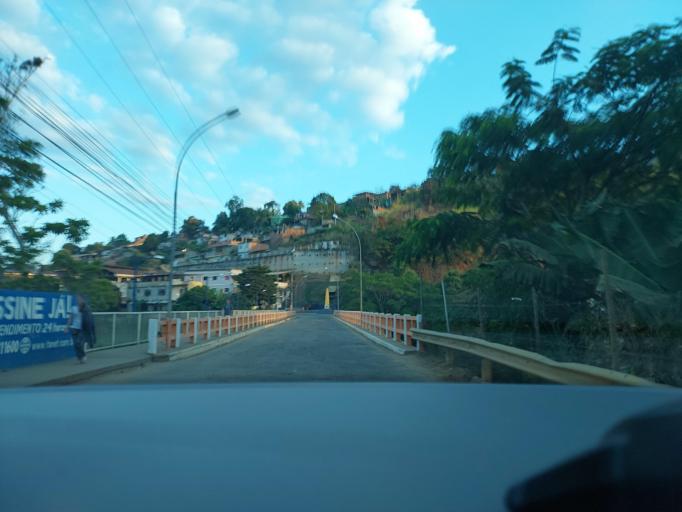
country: BR
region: Rio de Janeiro
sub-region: Miracema
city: Miracema
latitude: -21.2035
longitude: -42.1244
